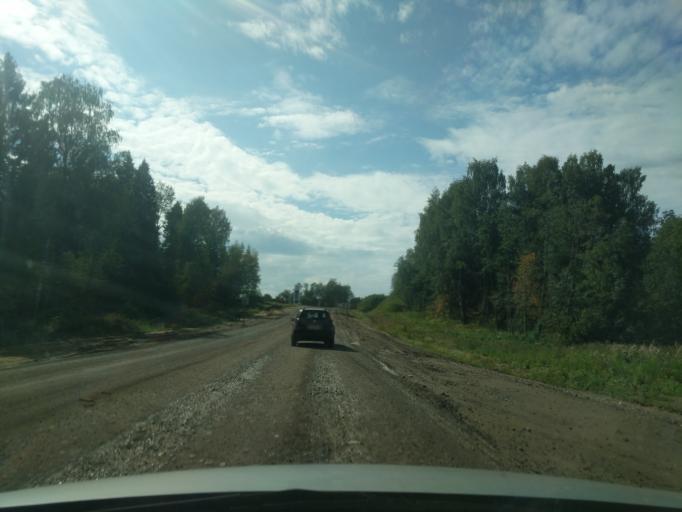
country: RU
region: Kostroma
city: Sudislavl'
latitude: 57.8760
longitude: 41.6775
